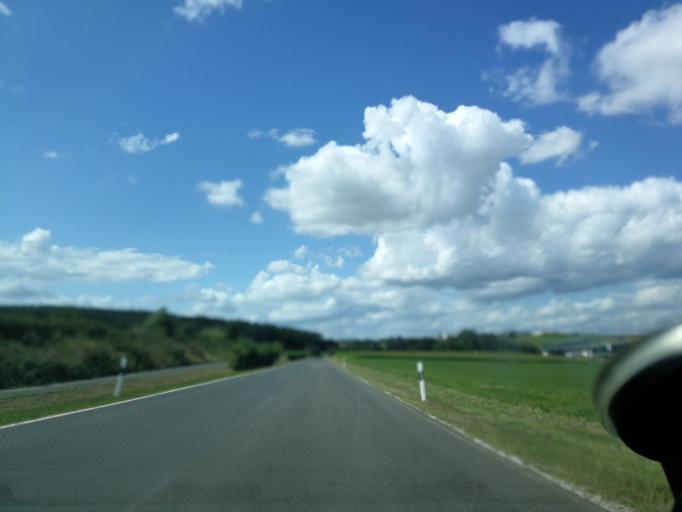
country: DE
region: Rheinland-Pfalz
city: Arenrath
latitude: 49.9627
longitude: 6.7336
